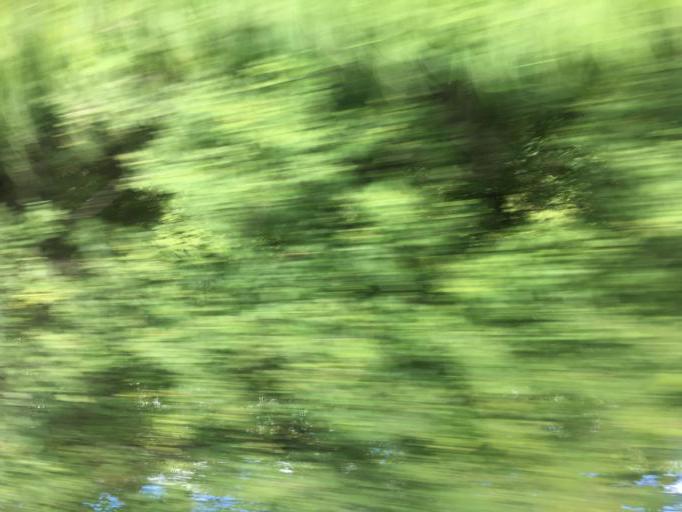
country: GB
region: Wales
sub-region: Carmarthenshire
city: Llansadwrn
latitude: 51.9699
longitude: -3.8756
